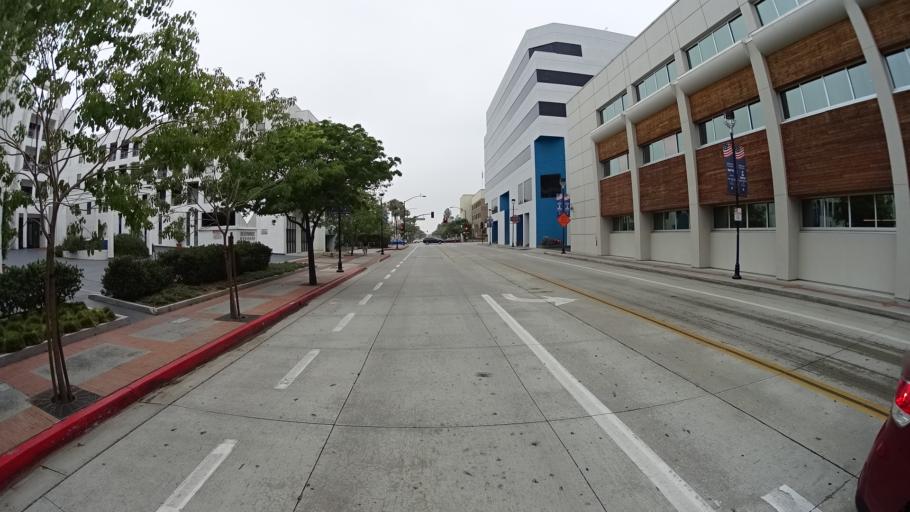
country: US
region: California
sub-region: Los Angeles County
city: Burbank
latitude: 34.1836
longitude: -118.3097
